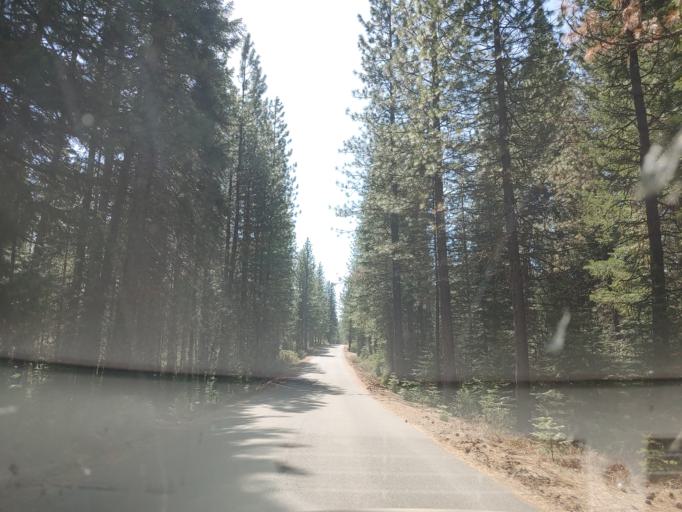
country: US
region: California
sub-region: Siskiyou County
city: McCloud
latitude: 41.2431
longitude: -122.0073
